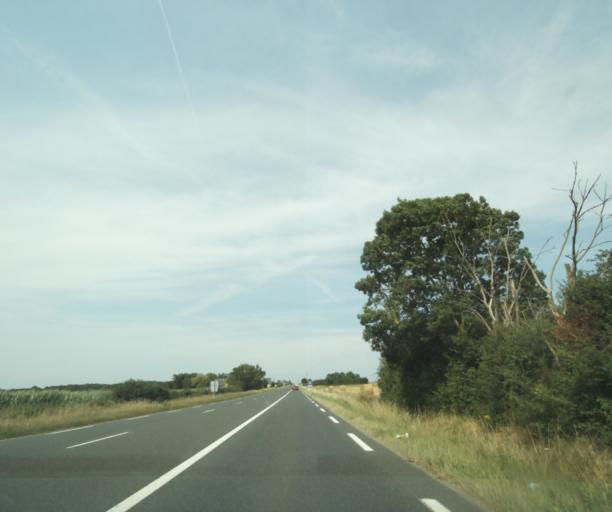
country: FR
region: Centre
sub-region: Departement d'Indre-et-Loire
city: Sorigny
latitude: 47.1883
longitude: 0.6638
